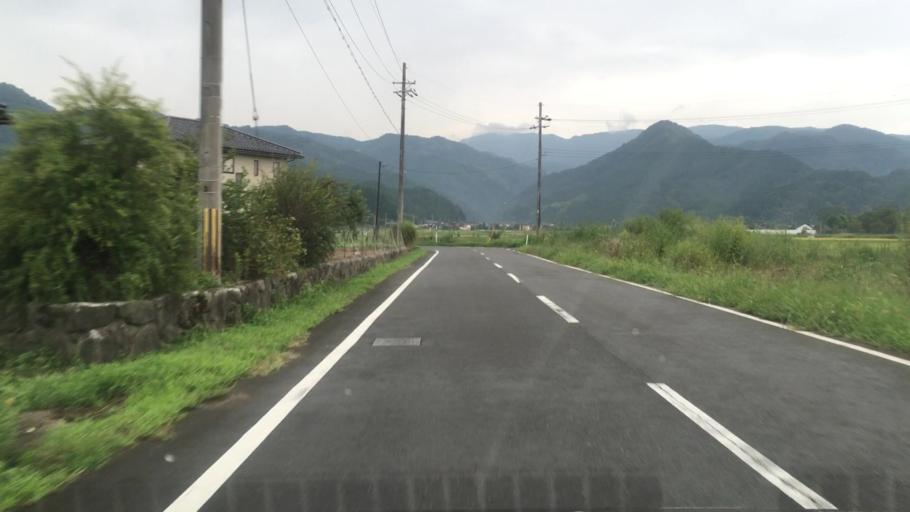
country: JP
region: Hyogo
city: Toyooka
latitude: 35.4550
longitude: 134.7348
